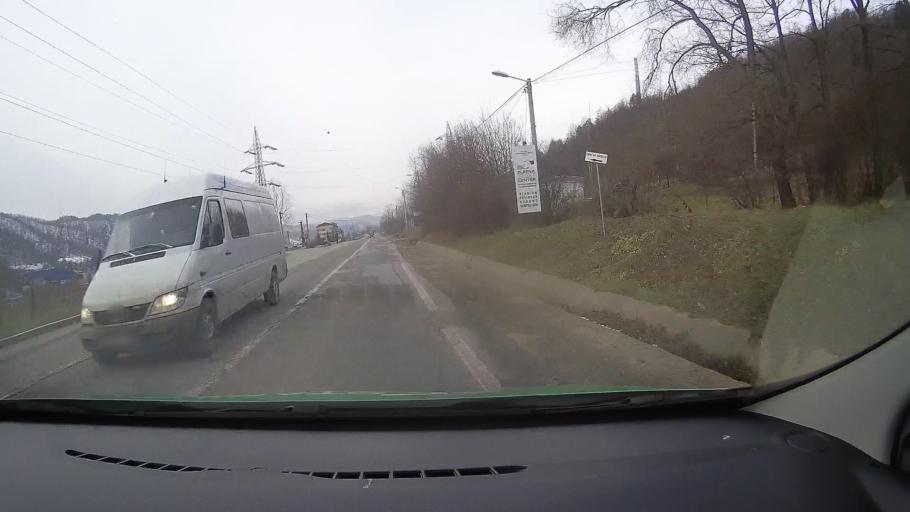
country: RO
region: Alba
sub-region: Oras Zlatna
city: Zlatna
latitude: 46.1052
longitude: 23.2430
